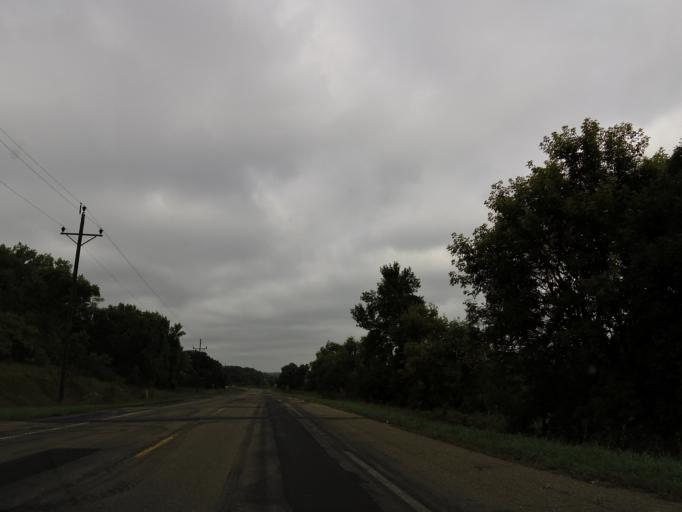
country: US
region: Minnesota
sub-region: Yellow Medicine County
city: Granite Falls
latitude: 44.8481
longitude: -95.6181
